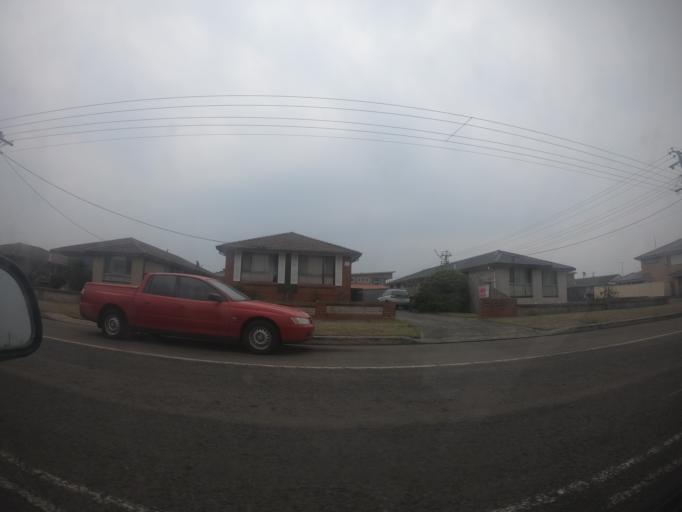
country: AU
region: New South Wales
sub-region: Shellharbour
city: Lake Illawarra
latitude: -34.5514
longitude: 150.8674
